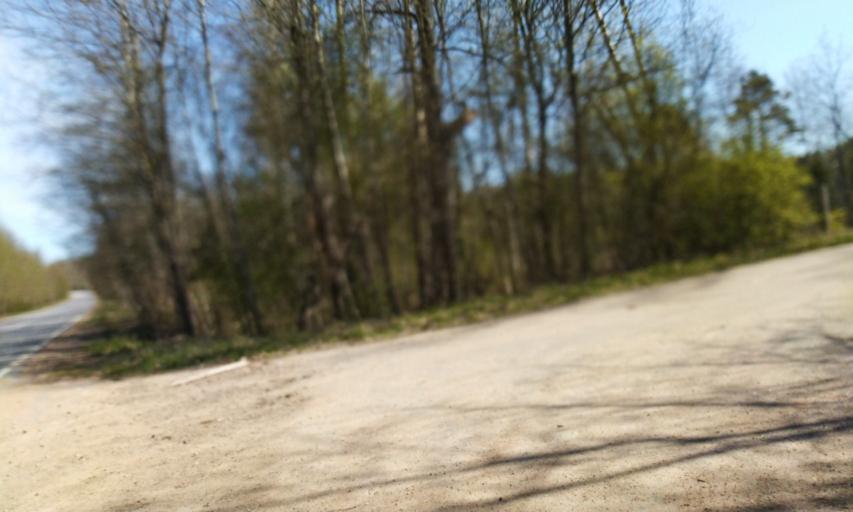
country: RU
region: Leningrad
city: Garbolovo
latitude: 60.4197
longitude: 30.4615
